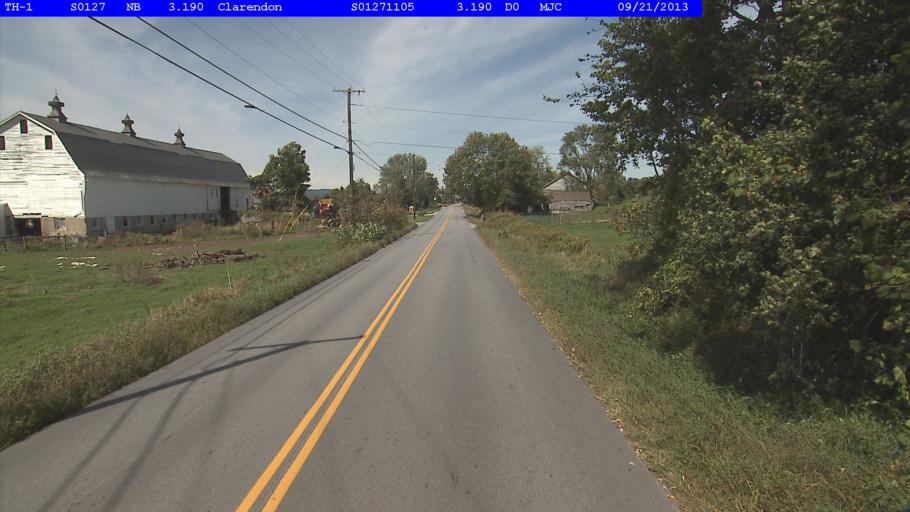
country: US
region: Vermont
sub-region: Rutland County
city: Rutland
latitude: 43.5593
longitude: -72.9719
